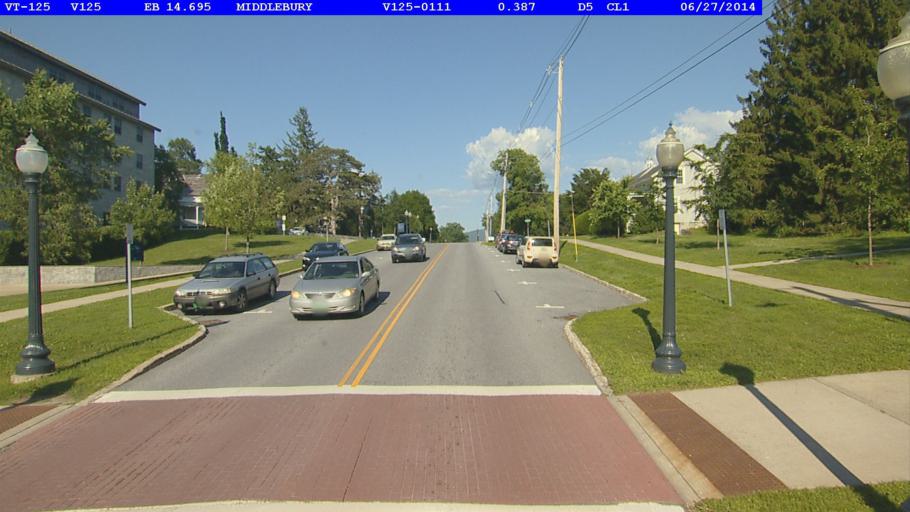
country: US
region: Vermont
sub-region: Addison County
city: Middlebury (village)
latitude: 44.0100
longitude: -73.1811
